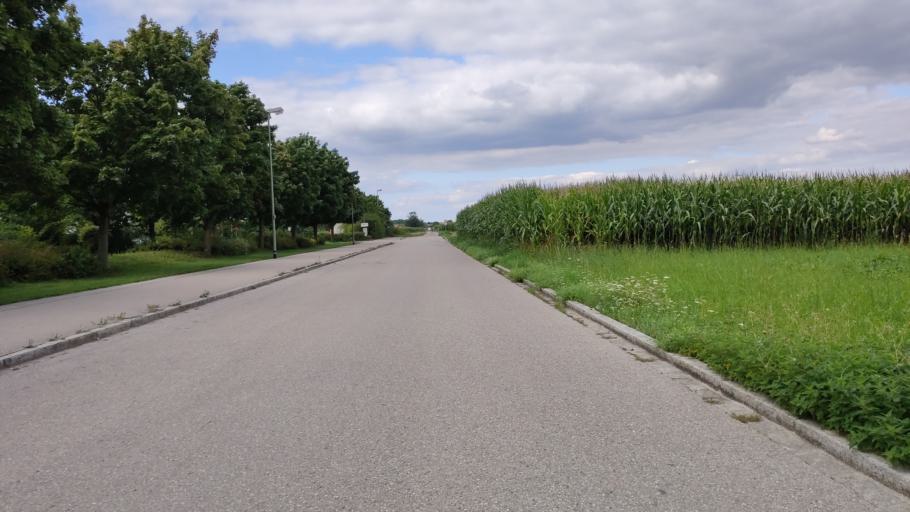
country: DE
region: Bavaria
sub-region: Swabia
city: Konigsbrunn
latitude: 48.2586
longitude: 10.8747
